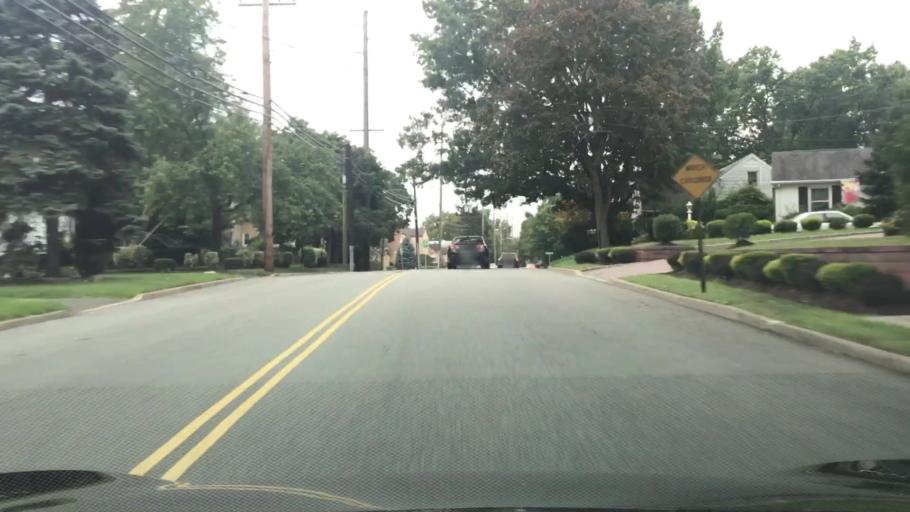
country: US
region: New Jersey
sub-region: Bergen County
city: Maywood
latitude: 40.9093
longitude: -74.0659
